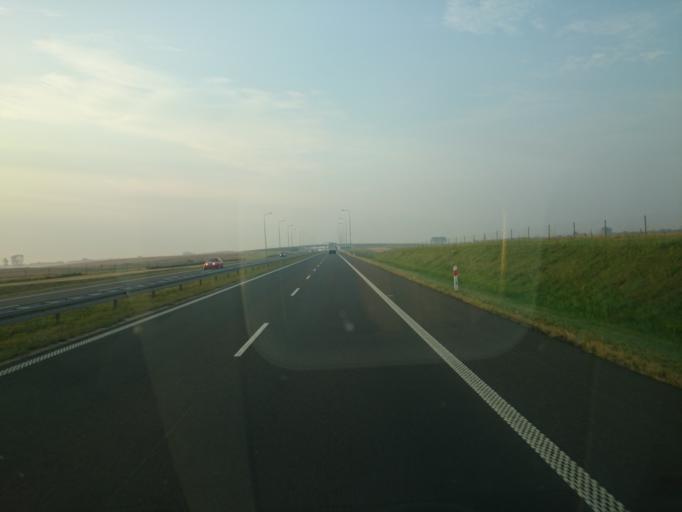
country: PL
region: West Pomeranian Voivodeship
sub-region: Powiat pyrzycki
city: Bielice
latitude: 53.1306
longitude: 14.7291
